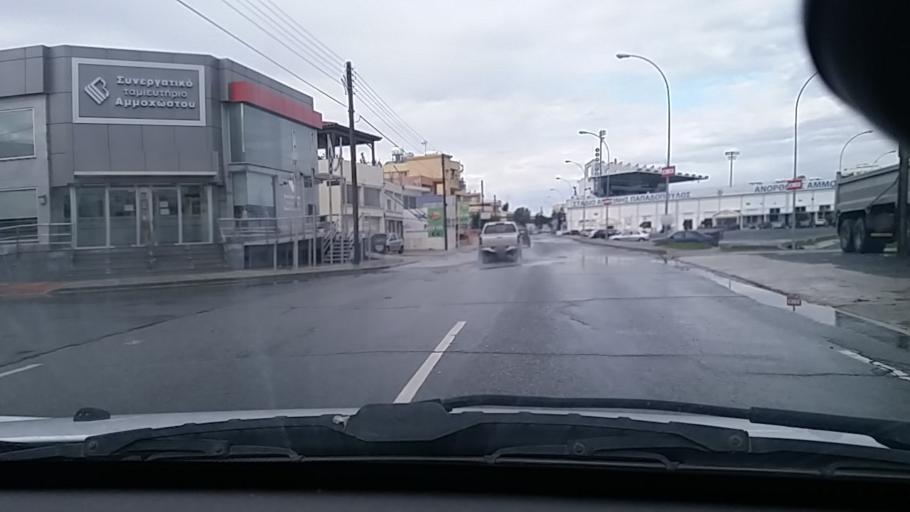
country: CY
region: Larnaka
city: Larnaca
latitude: 34.9349
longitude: 33.6214
